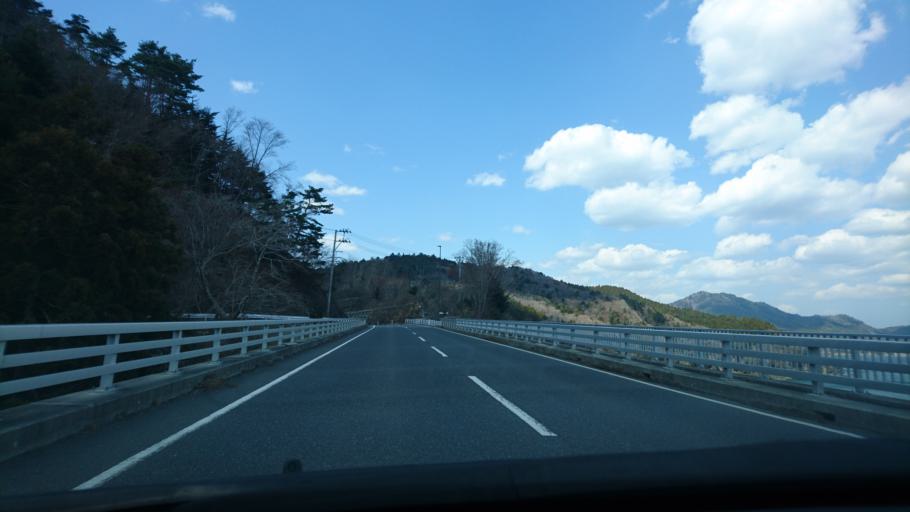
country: JP
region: Miyagi
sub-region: Oshika Gun
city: Onagawa Cho
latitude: 38.4850
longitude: 141.4921
